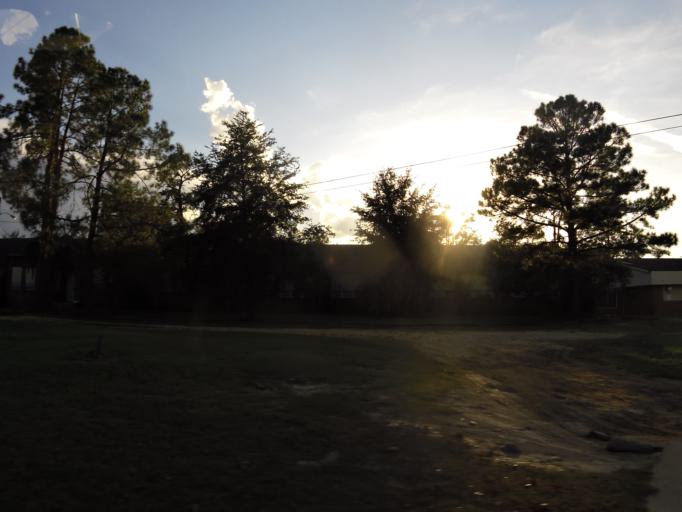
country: US
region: Georgia
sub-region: Lowndes County
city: Valdosta
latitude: 30.8208
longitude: -83.2689
